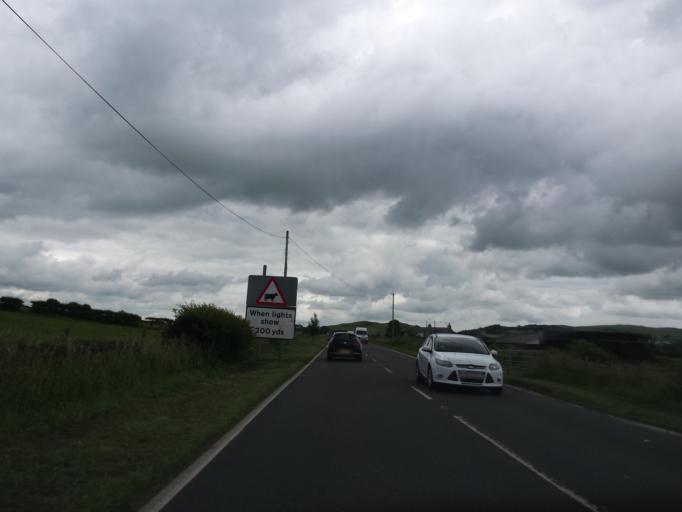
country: GB
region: Scotland
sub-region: Dumfries and Galloway
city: Dumfries
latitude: 55.0542
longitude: -3.7343
